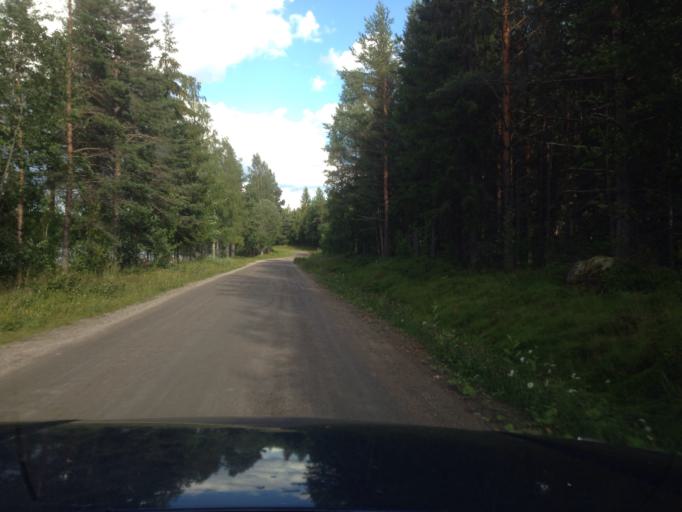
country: SE
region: Dalarna
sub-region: Ludvika Kommun
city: Abborrberget
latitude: 60.3114
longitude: 14.6607
